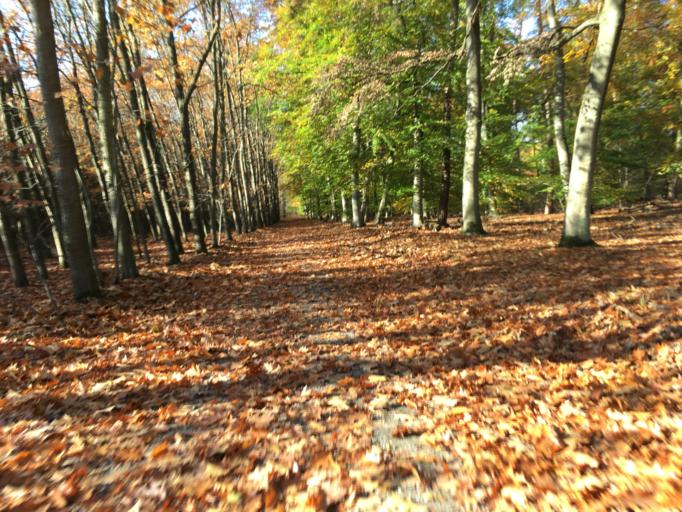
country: DE
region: Hesse
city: Lorsch
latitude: 49.6469
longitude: 8.5463
